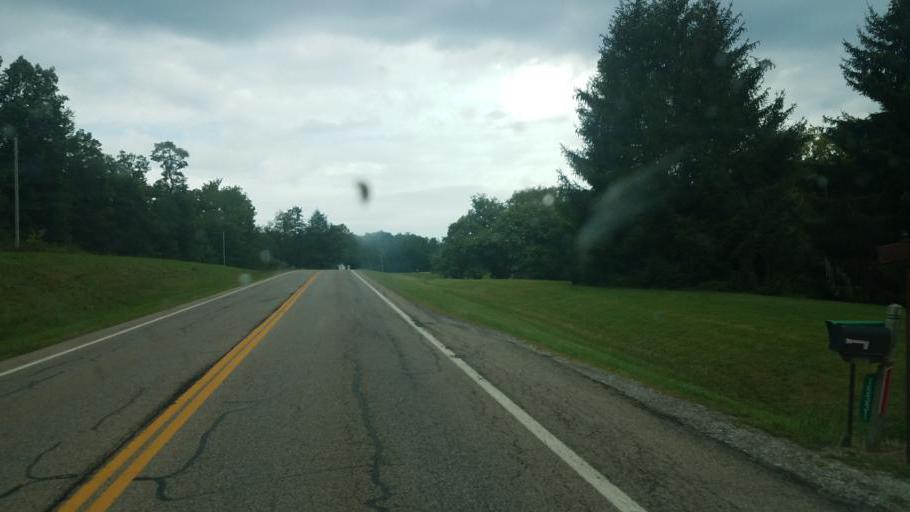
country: US
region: Ohio
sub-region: Knox County
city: Gambier
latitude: 40.4563
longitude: -82.4159
